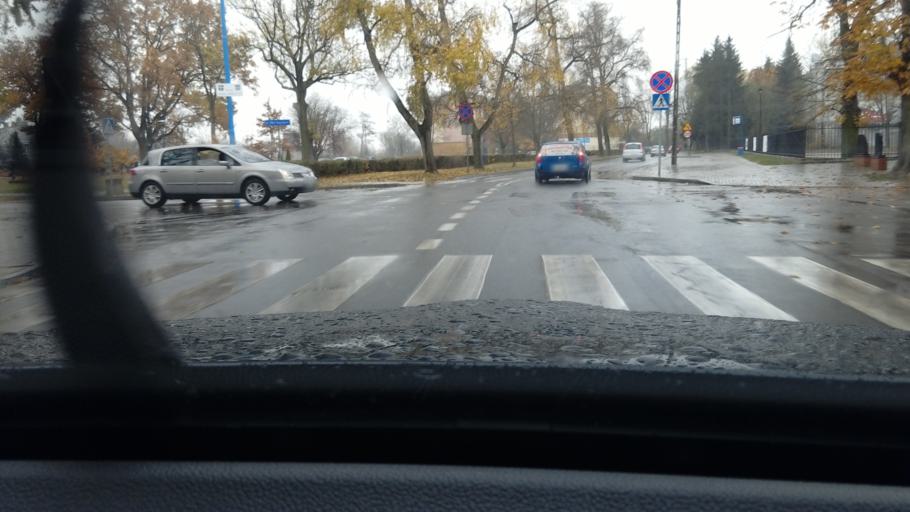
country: PL
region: Lodz Voivodeship
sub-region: Skierniewice
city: Skierniewice
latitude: 51.9493
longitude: 20.1436
